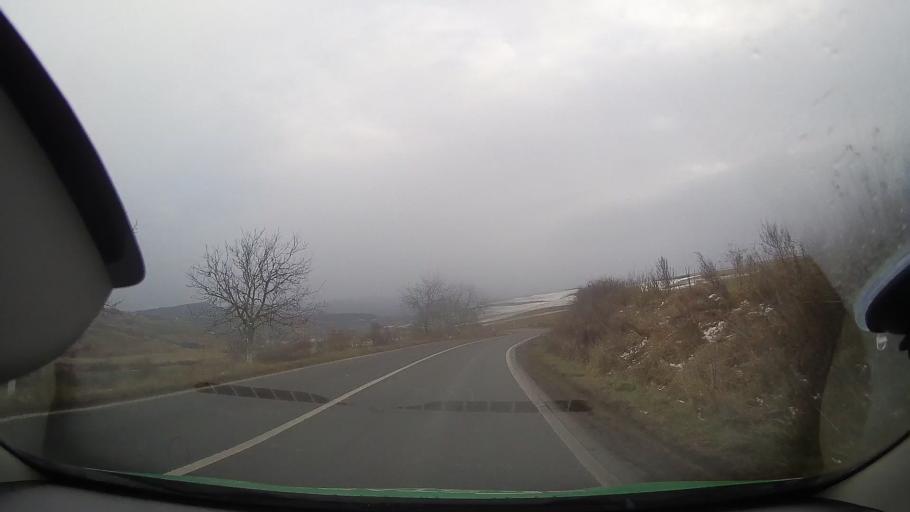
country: RO
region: Sibiu
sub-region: Comuna Blajel
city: Blajel
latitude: 46.2427
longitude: 24.3020
